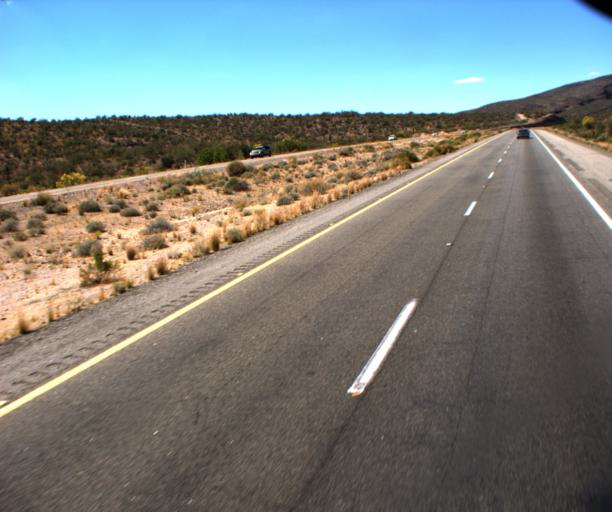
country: US
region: Arizona
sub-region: Yavapai County
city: Bagdad
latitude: 34.5583
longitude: -113.4551
